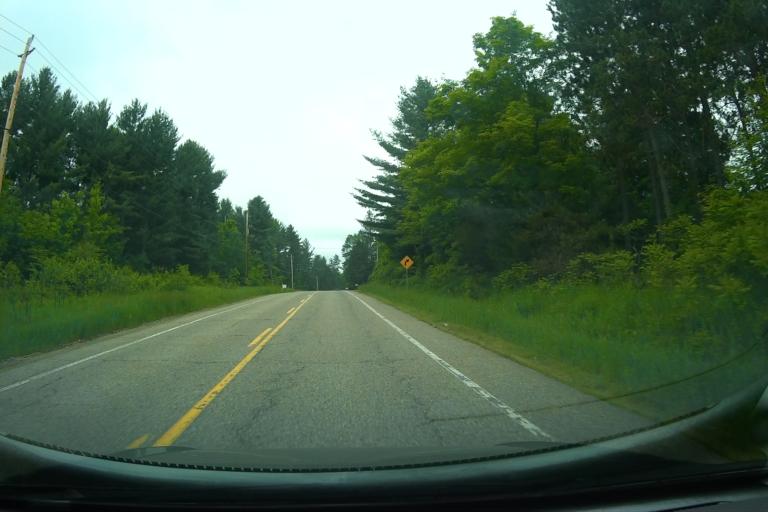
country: CA
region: Ontario
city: Pembroke
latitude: 45.4929
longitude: -77.1733
